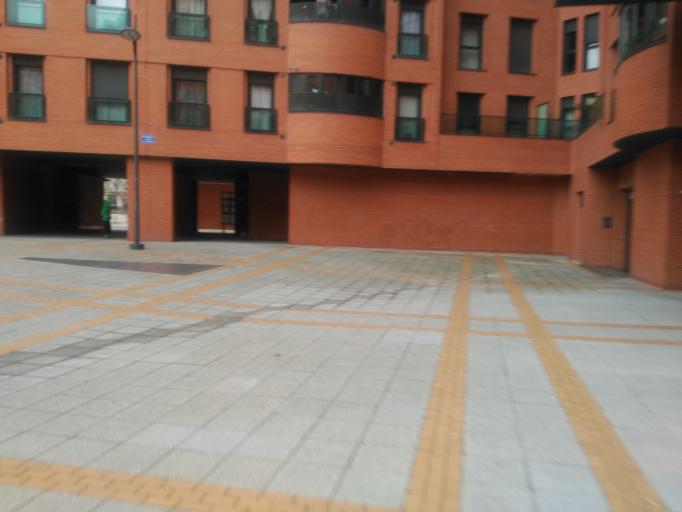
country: ES
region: Castille and Leon
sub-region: Provincia de Burgos
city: Burgos
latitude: 42.3344
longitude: -3.7016
